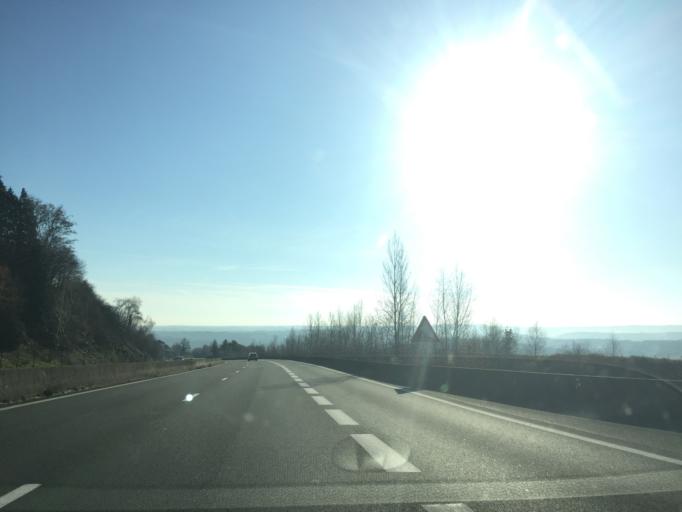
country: FR
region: Limousin
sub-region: Departement de la Correze
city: Donzenac
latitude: 45.2386
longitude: 1.5126
